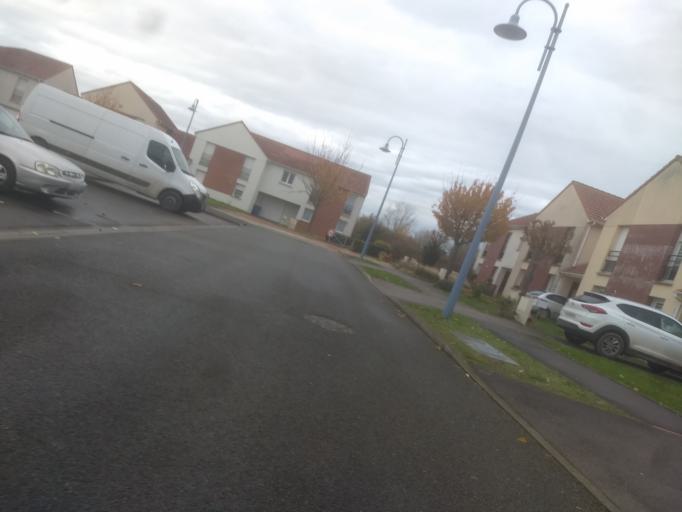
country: FR
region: Nord-Pas-de-Calais
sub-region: Departement du Pas-de-Calais
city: Dainville
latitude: 50.2854
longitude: 2.7206
